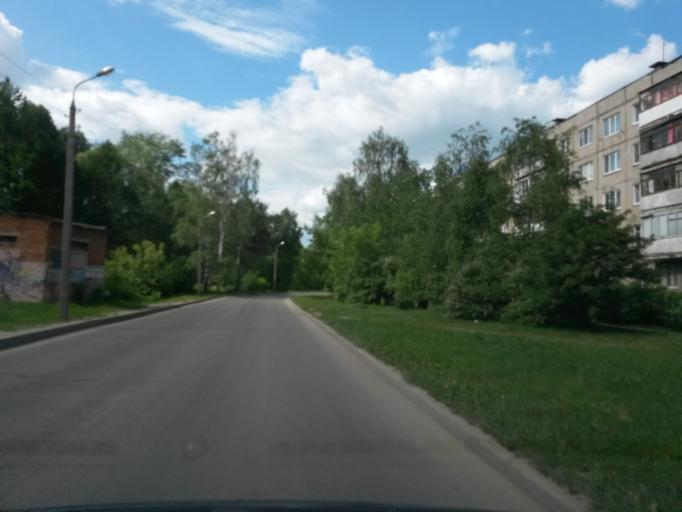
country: RU
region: Jaroslavl
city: Yaroslavl
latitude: 57.6443
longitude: 39.9419
